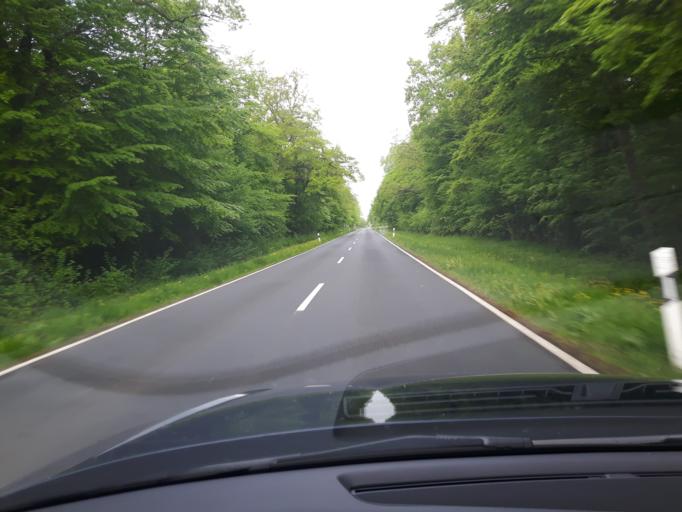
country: DE
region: Mecklenburg-Vorpommern
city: Velgast
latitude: 54.2554
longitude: 12.7183
